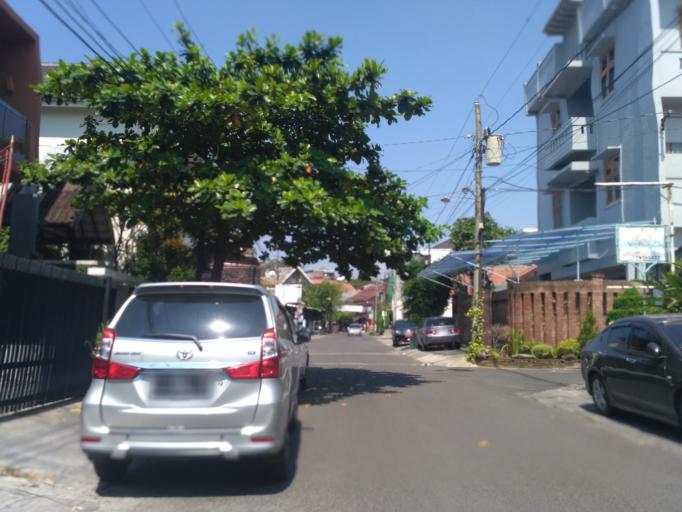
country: ID
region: Central Java
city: Semarang
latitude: -6.9990
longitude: 110.4259
